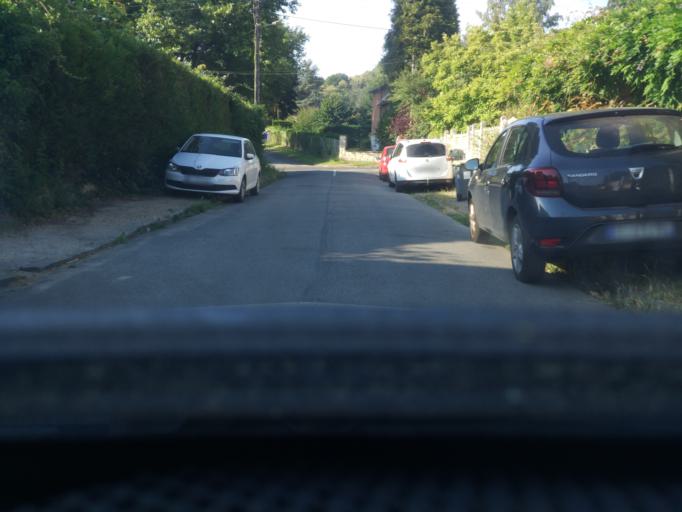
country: FR
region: Ile-de-France
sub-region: Departement des Yvelines
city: Saint-Remy-les-Chevreuse
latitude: 48.6954
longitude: 2.0611
